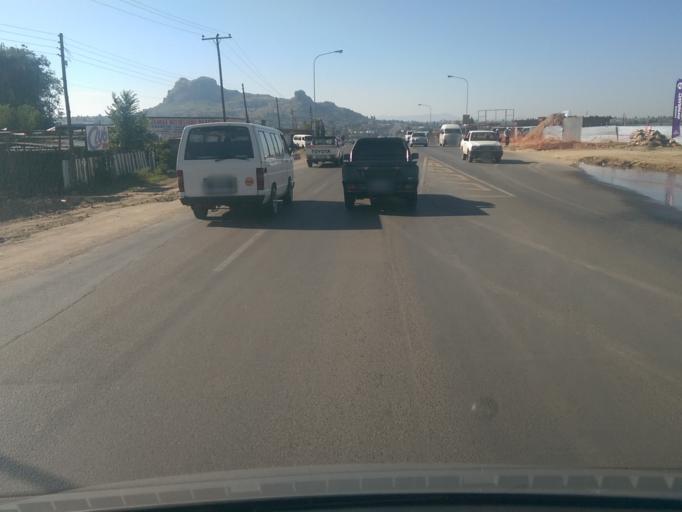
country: LS
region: Maseru
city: Maseru
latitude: -29.3370
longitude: 27.5109
